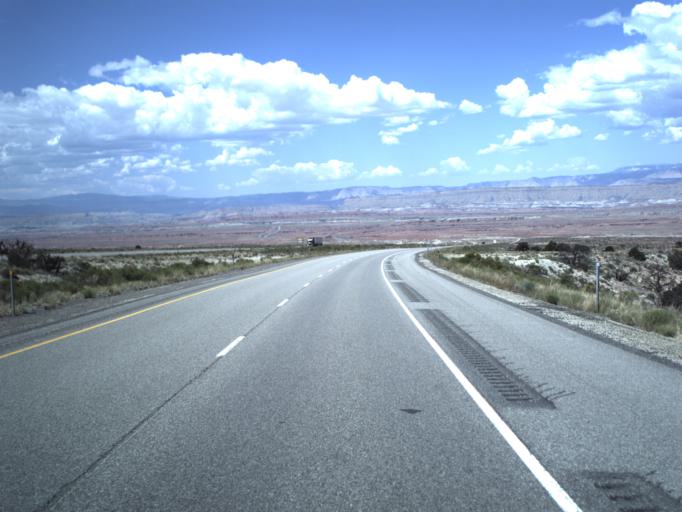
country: US
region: Utah
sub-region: Emery County
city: Ferron
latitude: 38.8416
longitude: -110.9604
